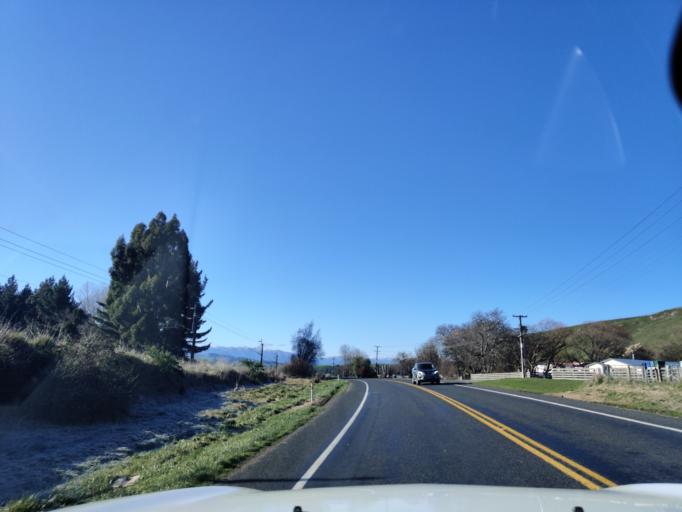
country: NZ
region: Manawatu-Wanganui
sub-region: Ruapehu District
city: Waiouru
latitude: -39.6900
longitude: 175.8092
